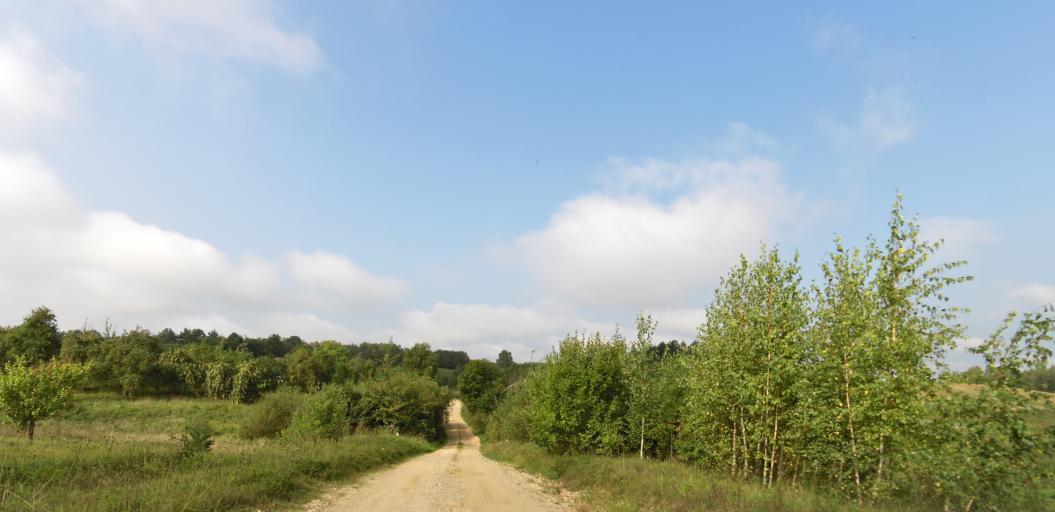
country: LT
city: Grigiskes
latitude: 54.7719
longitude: 25.0663
